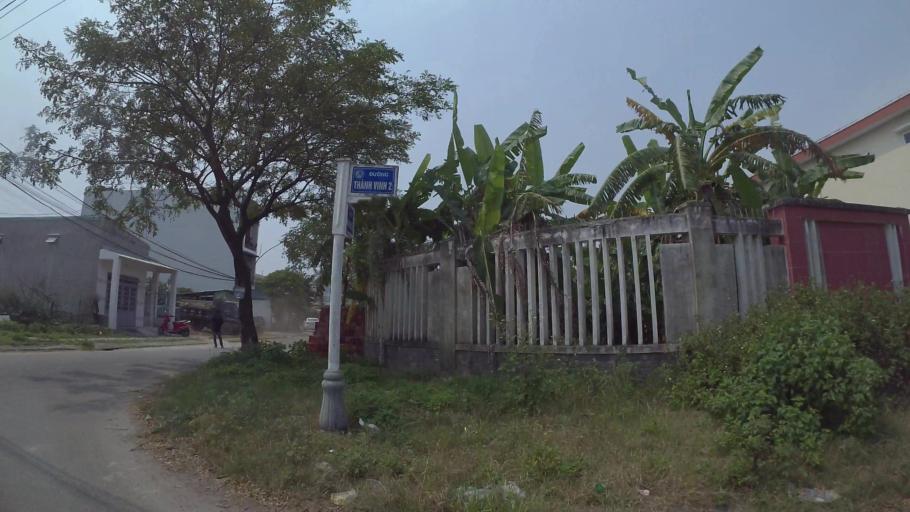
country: VN
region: Da Nang
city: Son Tra
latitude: 16.1045
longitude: 108.2545
